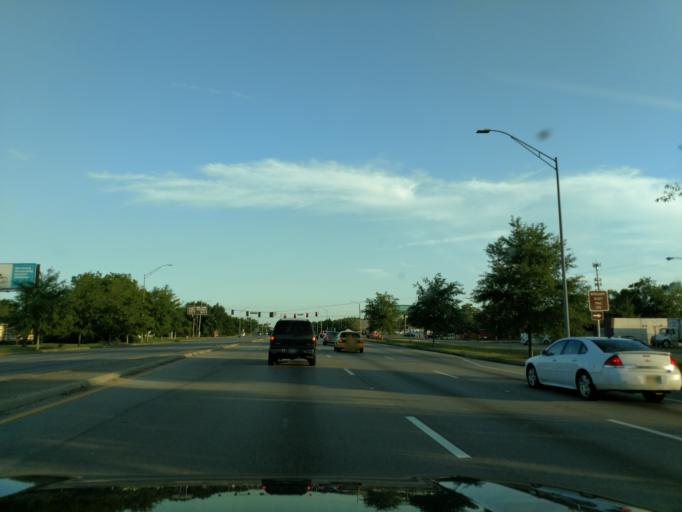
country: US
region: Mississippi
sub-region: Harrison County
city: West Gulfport
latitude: 30.4055
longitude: -89.0929
